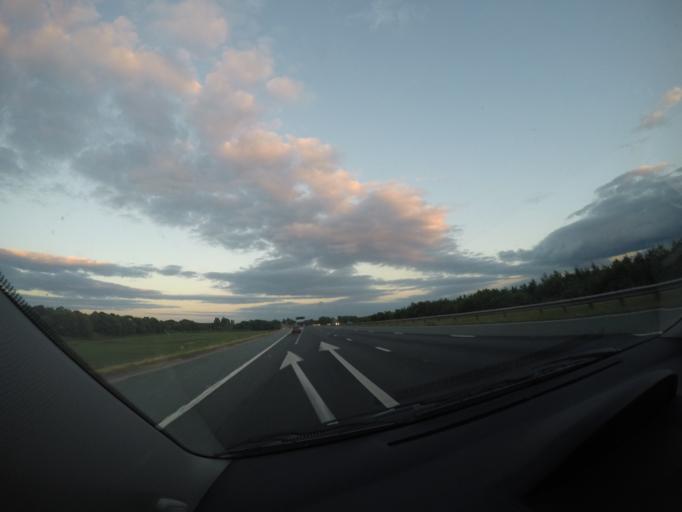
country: GB
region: England
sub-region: North Yorkshire
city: Boroughbridge
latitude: 54.0145
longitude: -1.3798
